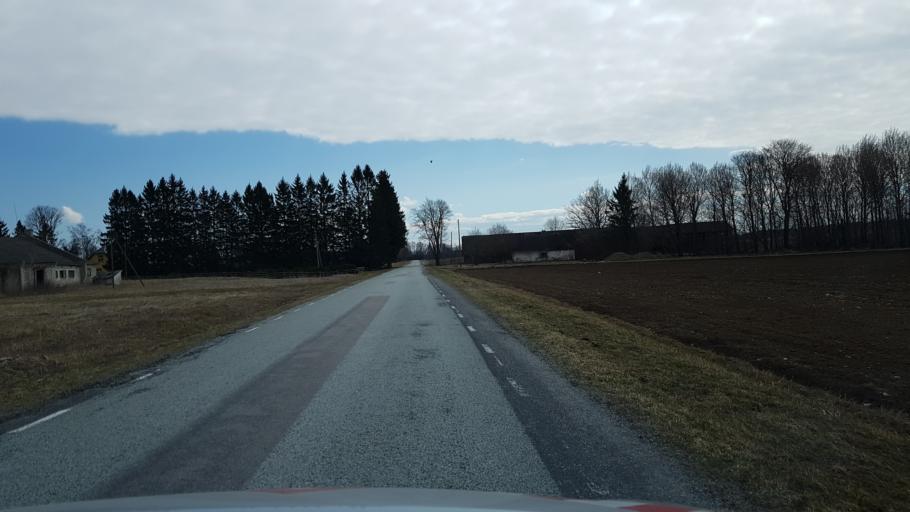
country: EE
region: Laeaene-Virumaa
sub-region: Haljala vald
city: Haljala
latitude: 59.4192
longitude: 26.2404
